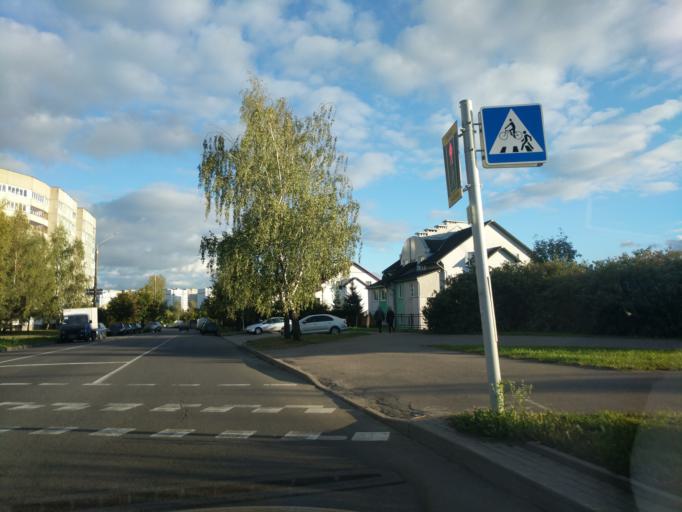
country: BY
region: Minsk
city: Malinovka
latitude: 53.8571
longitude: 27.4563
